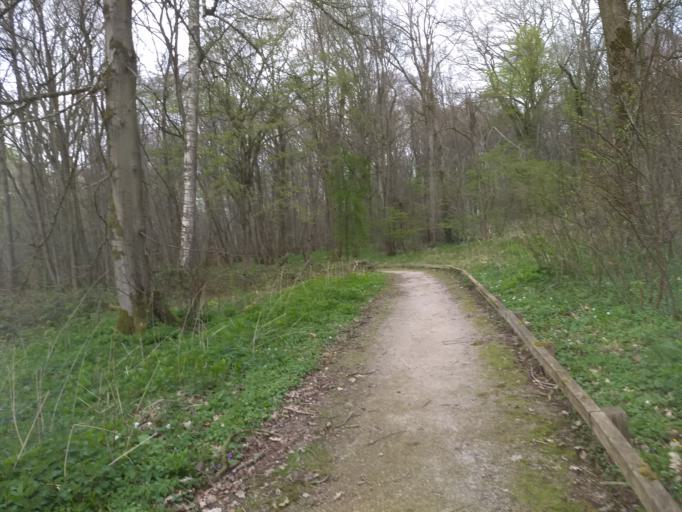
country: FR
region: Nord-Pas-de-Calais
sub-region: Departement du Pas-de-Calais
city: Maroeuil
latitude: 50.3351
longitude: 2.6969
